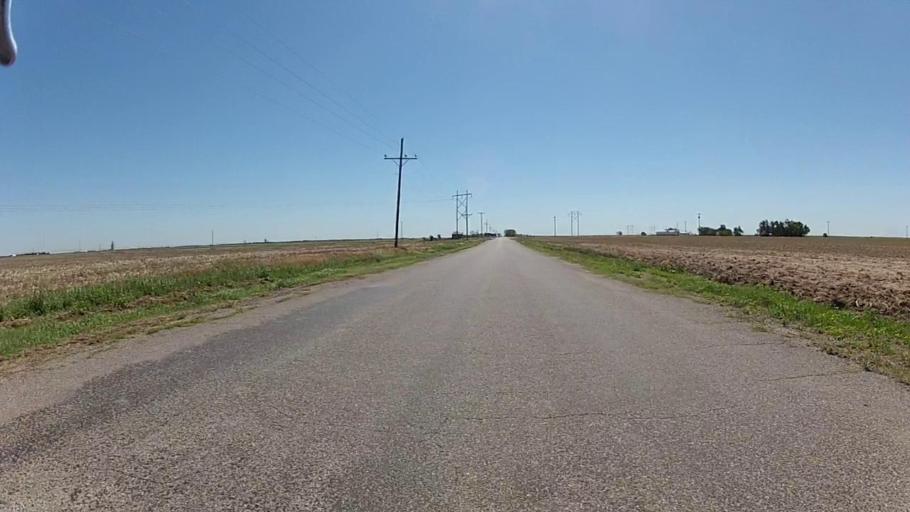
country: US
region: Kansas
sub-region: Kiowa County
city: Greensburg
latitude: 37.5866
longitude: -99.3418
